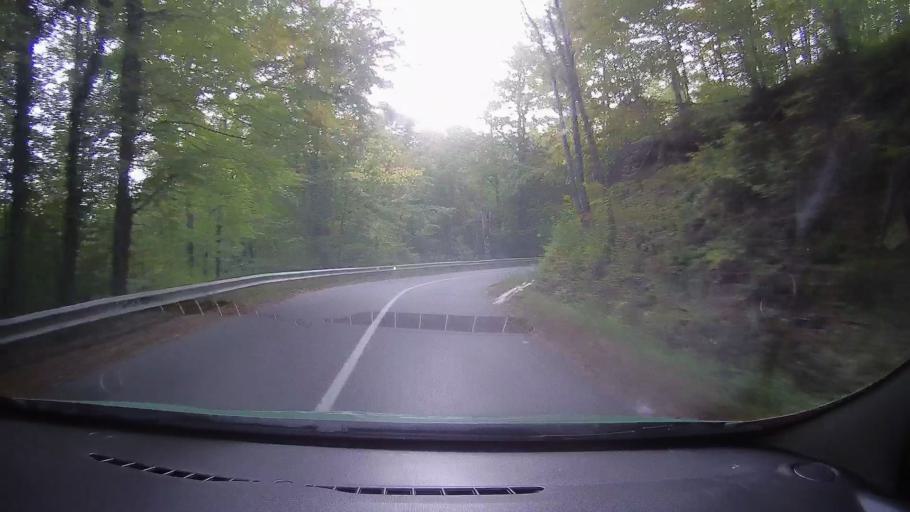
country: RO
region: Timis
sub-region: Comuna Nadrag
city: Nadrag
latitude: 45.6755
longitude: 22.1761
